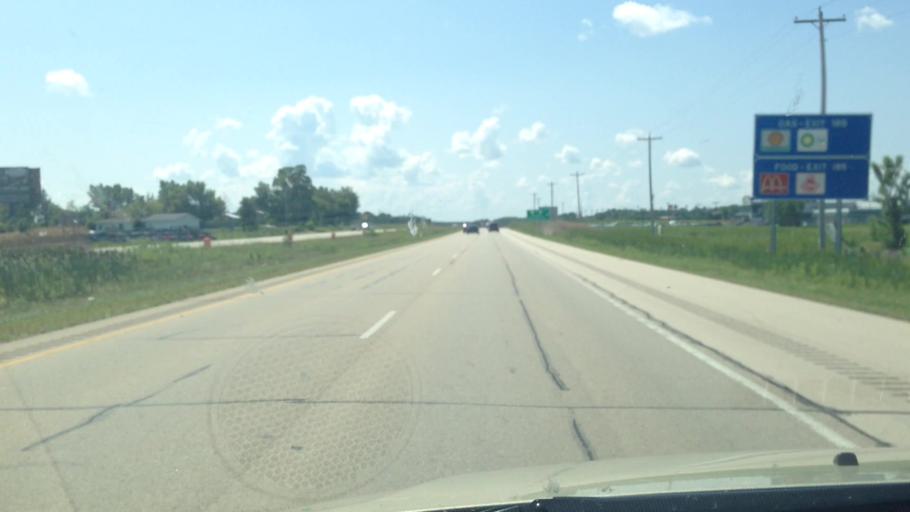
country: US
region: Wisconsin
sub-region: Oconto County
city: Oconto Falls
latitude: 44.7722
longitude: -88.0507
